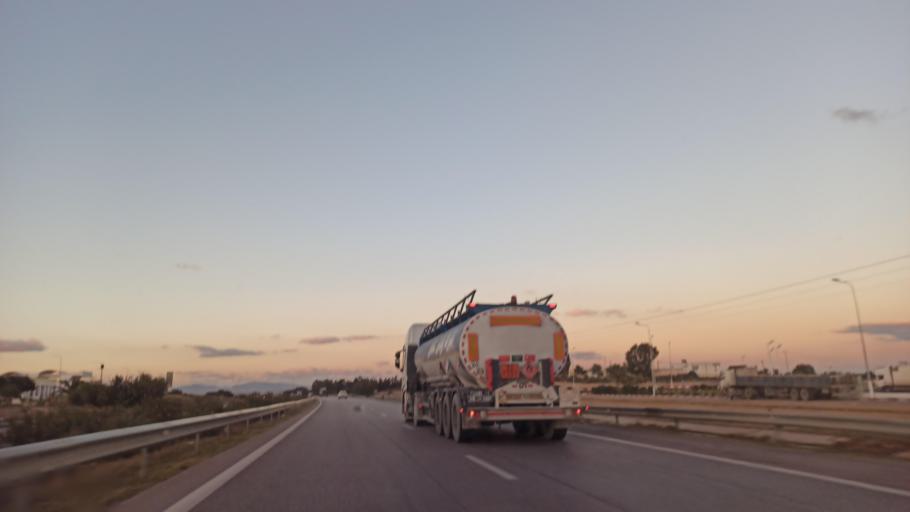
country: TN
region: Susah
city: Harqalah
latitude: 36.2474
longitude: 10.4241
